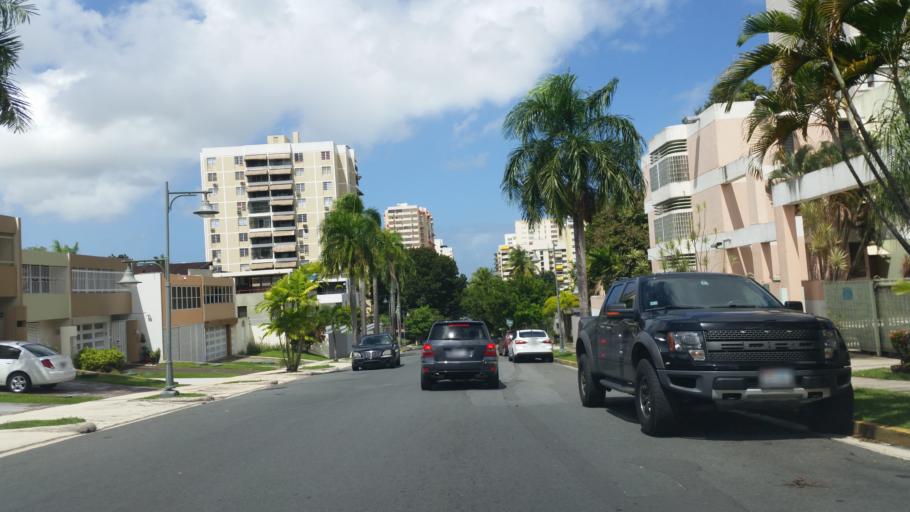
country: PR
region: Catano
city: Catano
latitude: 18.4012
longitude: -66.0986
